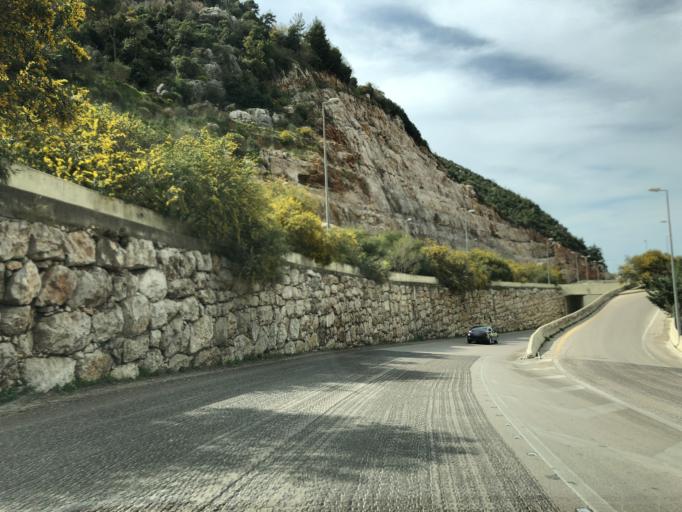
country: LB
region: Mont-Liban
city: Jdaidet el Matn
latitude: 33.8954
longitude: 35.6510
